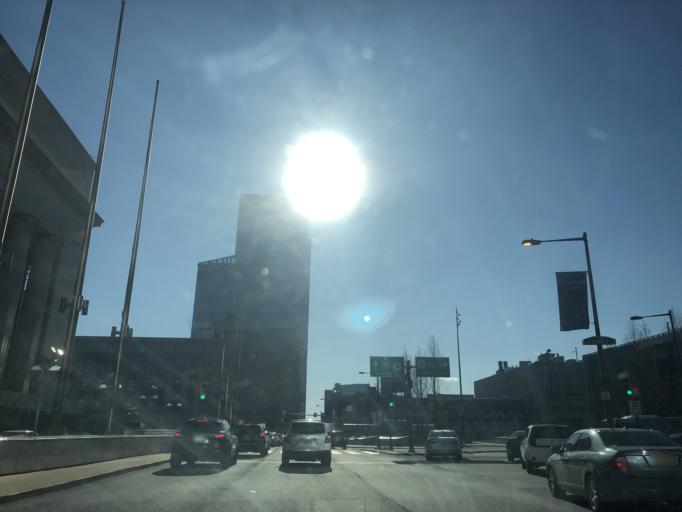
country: US
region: Pennsylvania
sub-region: Philadelphia County
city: Philadelphia
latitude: 39.9564
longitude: -75.1830
